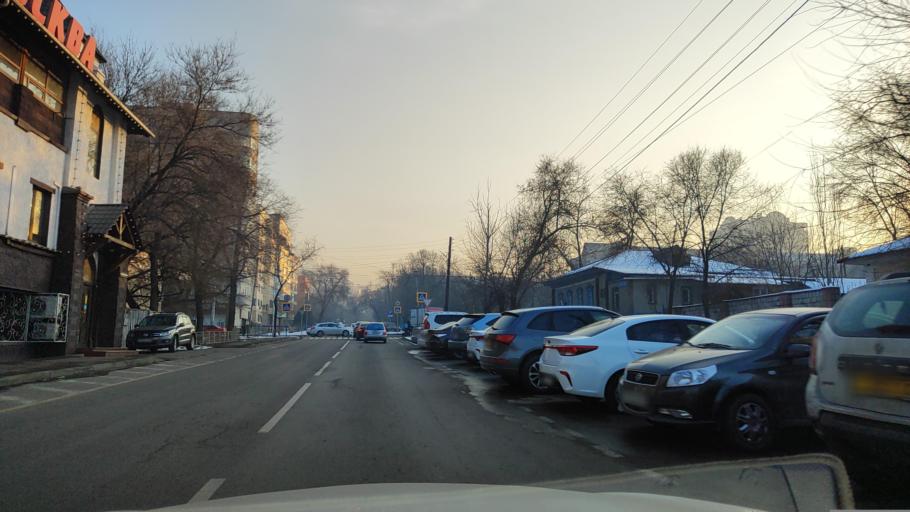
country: KZ
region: Almaty Qalasy
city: Almaty
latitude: 43.2565
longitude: 76.9602
